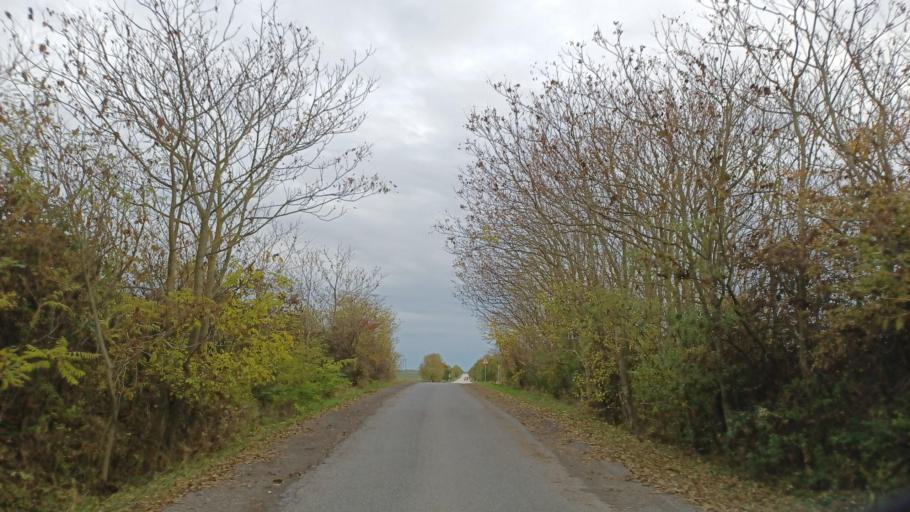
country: HU
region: Tolna
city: Nagydorog
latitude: 46.6818
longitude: 18.5991
